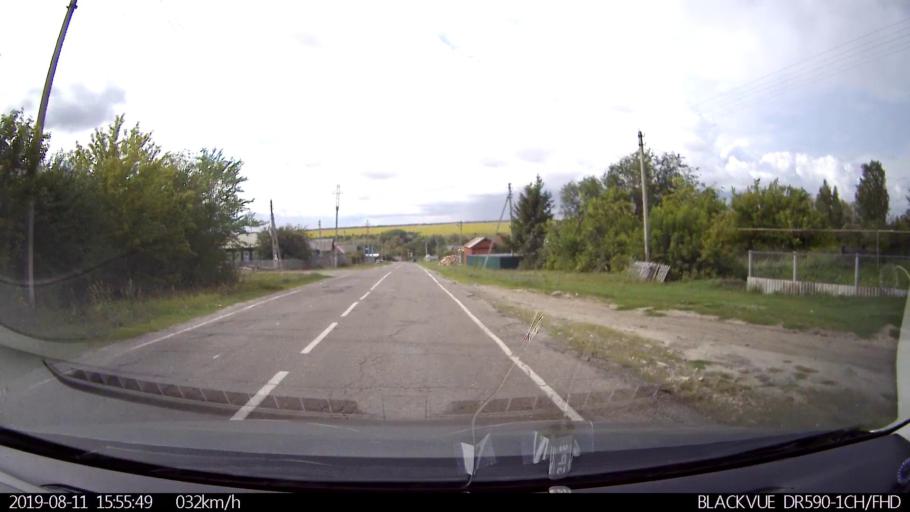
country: RU
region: Ulyanovsk
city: Ignatovka
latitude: 53.9465
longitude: 47.6521
